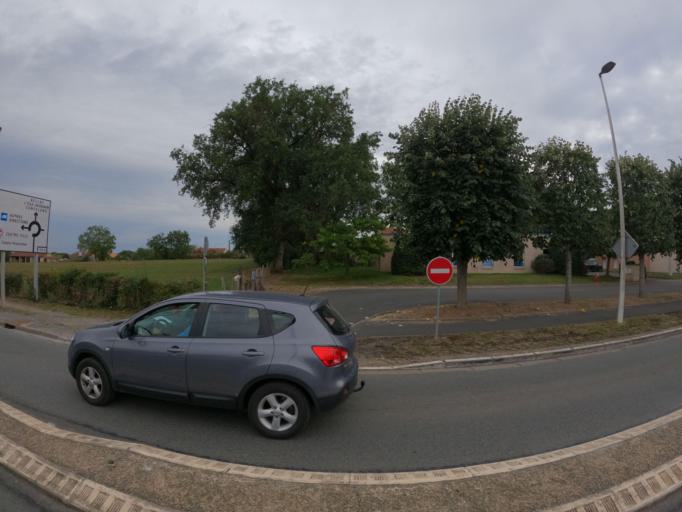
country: FR
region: Poitou-Charentes
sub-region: Departement de la Vienne
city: Montmorillon
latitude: 46.4205
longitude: 0.8573
